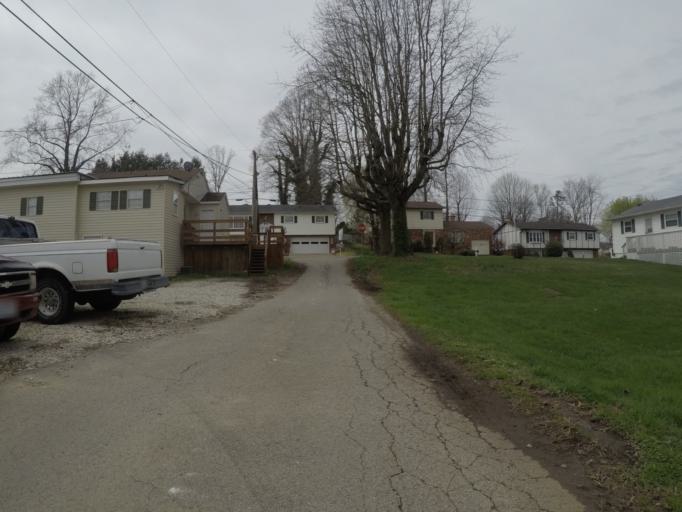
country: US
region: West Virginia
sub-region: Cabell County
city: Barboursville
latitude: 38.4208
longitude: -82.3041
